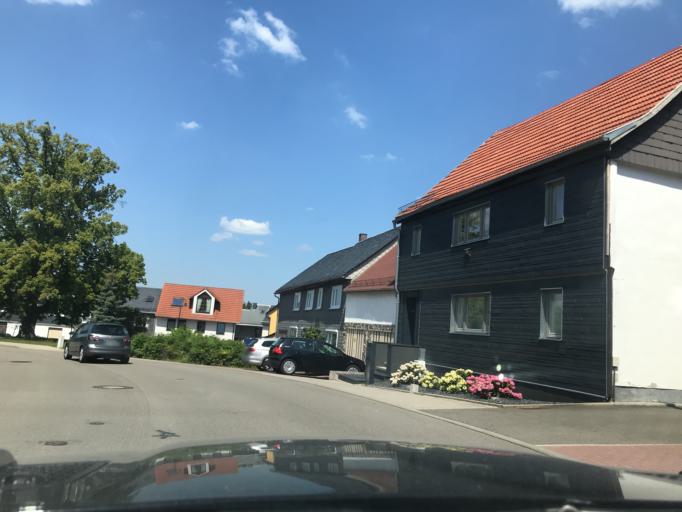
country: DE
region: Thuringia
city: Neuhaus
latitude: 50.7038
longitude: 10.9299
